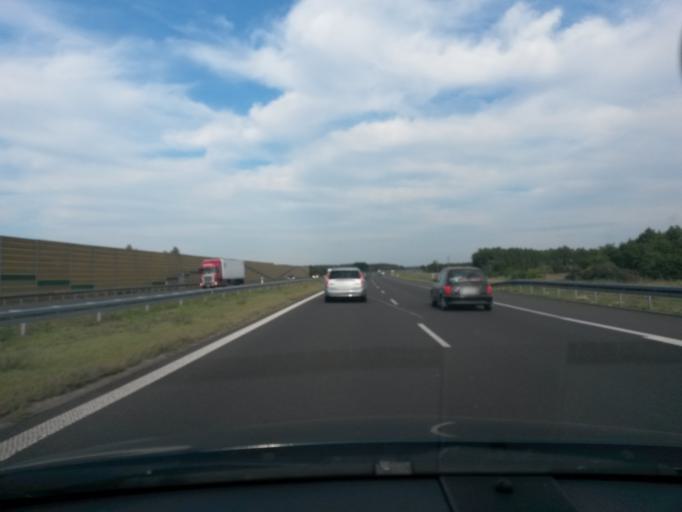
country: PL
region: Greater Poland Voivodeship
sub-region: Powiat koninski
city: Krzymow
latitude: 52.1526
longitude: 18.4646
